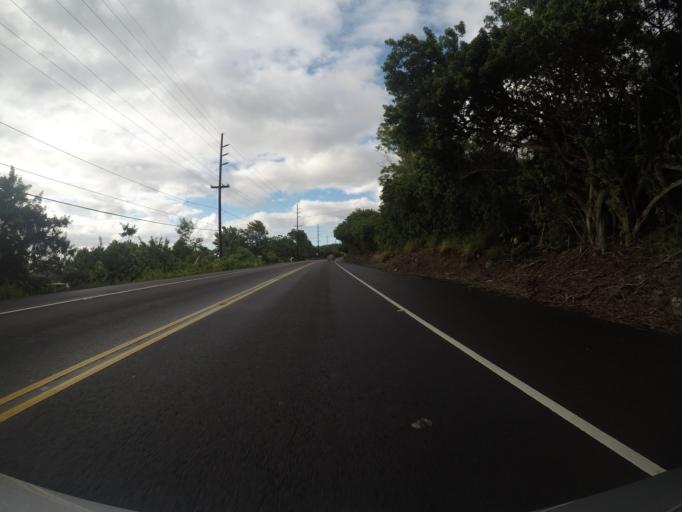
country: US
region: Hawaii
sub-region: Hawaii County
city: Kalaoa
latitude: 19.7373
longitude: -155.9772
